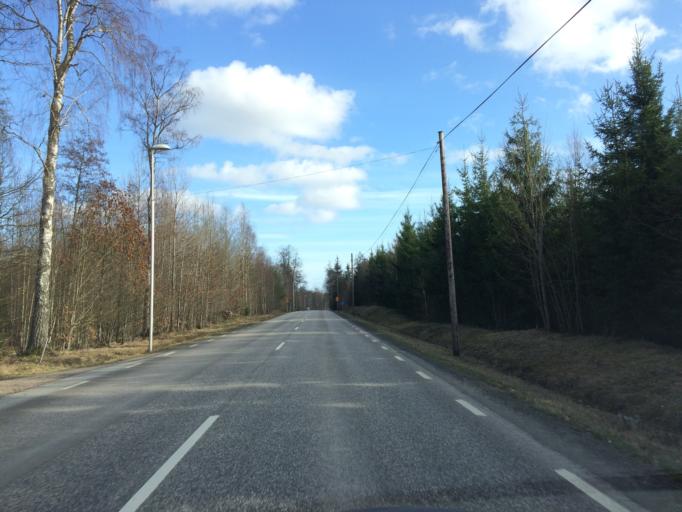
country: SE
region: Kronoberg
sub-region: Almhults Kommun
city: AElmhult
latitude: 56.5688
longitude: 14.1218
